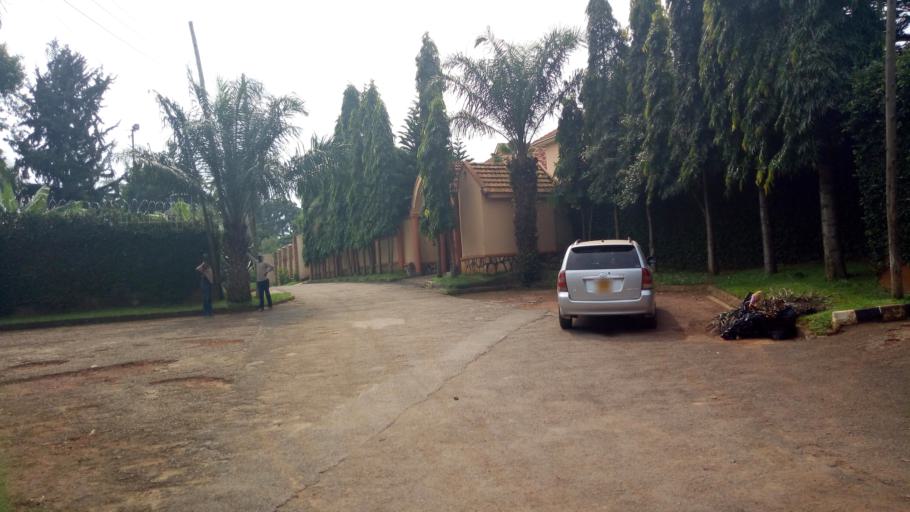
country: UG
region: Central Region
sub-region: Kampala District
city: Kampala
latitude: 0.3108
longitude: 32.6228
